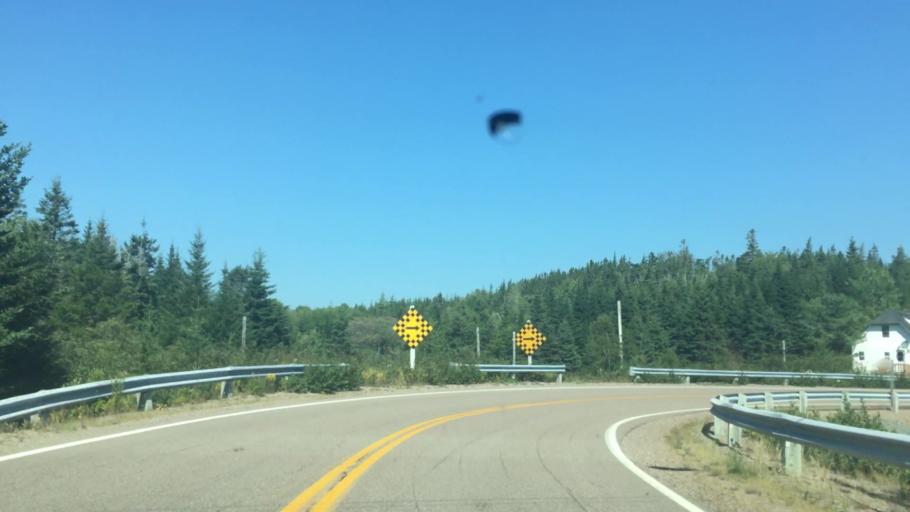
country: CA
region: Nova Scotia
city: Antigonish
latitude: 45.0276
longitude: -62.0310
